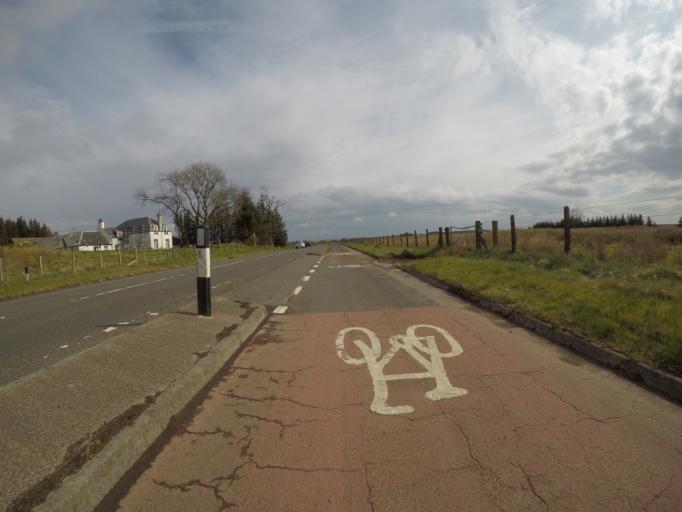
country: GB
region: Scotland
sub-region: East Renfrewshire
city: Neilston
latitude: 55.7064
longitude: -4.3982
